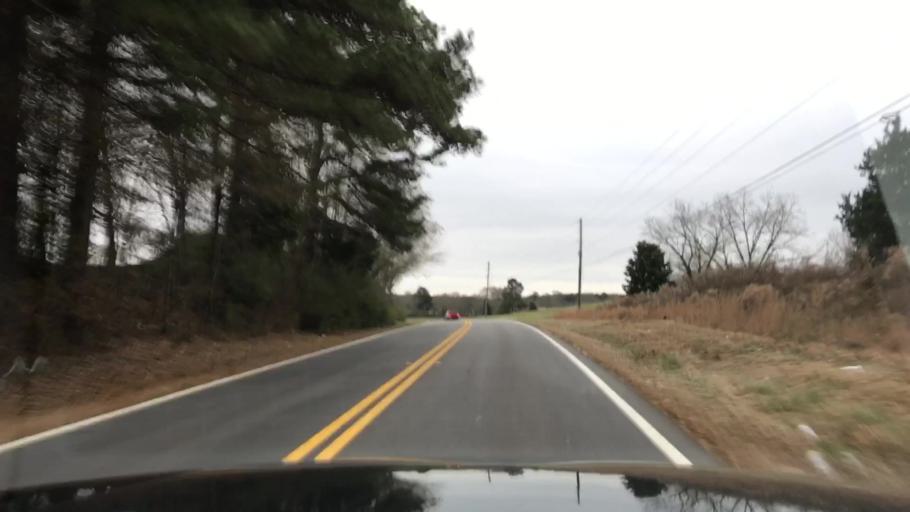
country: US
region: Georgia
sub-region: Barrow County
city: Auburn
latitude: 33.9066
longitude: -83.8144
